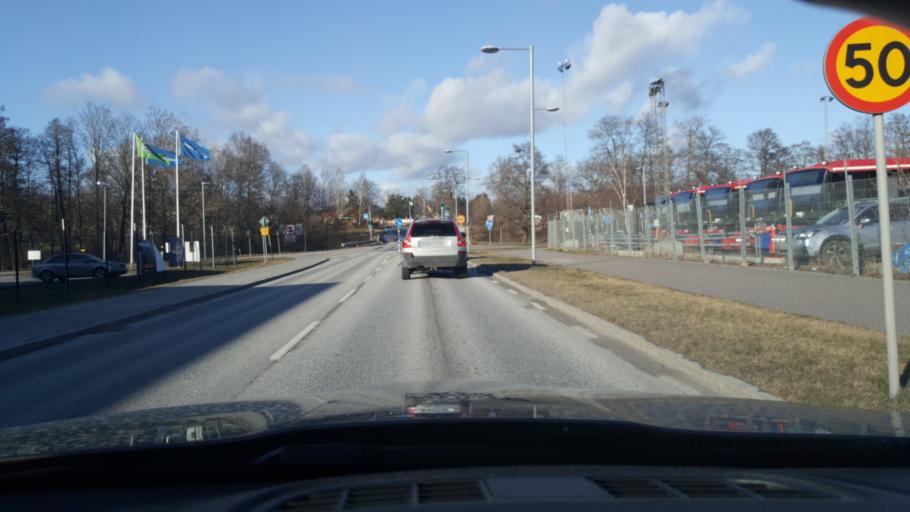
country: SE
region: Stockholm
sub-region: Osterakers Kommun
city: Akersberga
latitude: 59.4927
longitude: 18.2766
